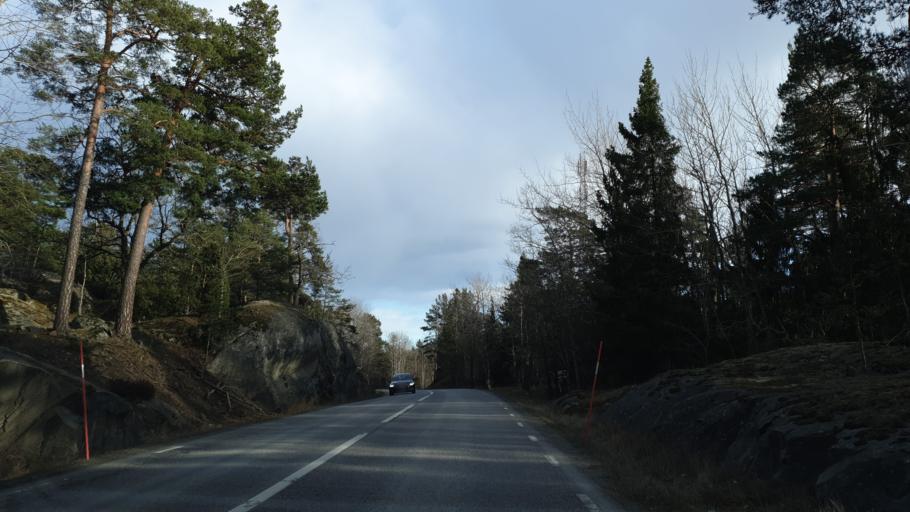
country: SE
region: Stockholm
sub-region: Varmdo Kommun
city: Holo
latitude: 59.3298
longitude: 18.7210
